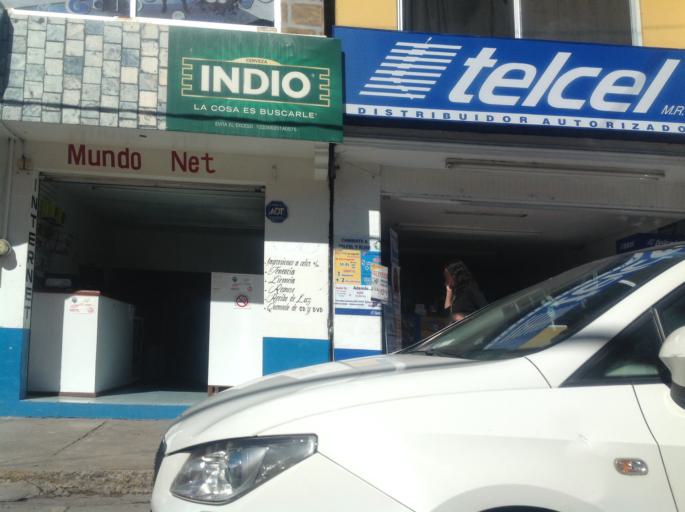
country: MX
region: Oaxaca
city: Ciudad de Huajuapam de Leon
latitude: 17.8054
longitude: -97.7760
